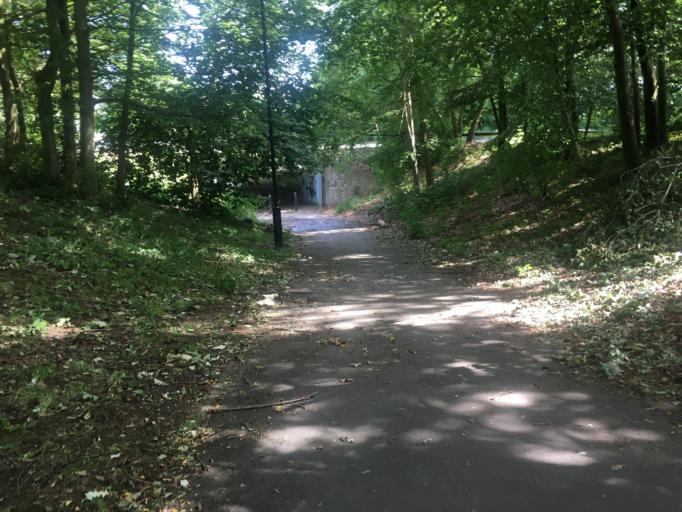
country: GB
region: England
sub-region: County Durham
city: Chester-le-Street
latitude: 54.8777
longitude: -1.5456
